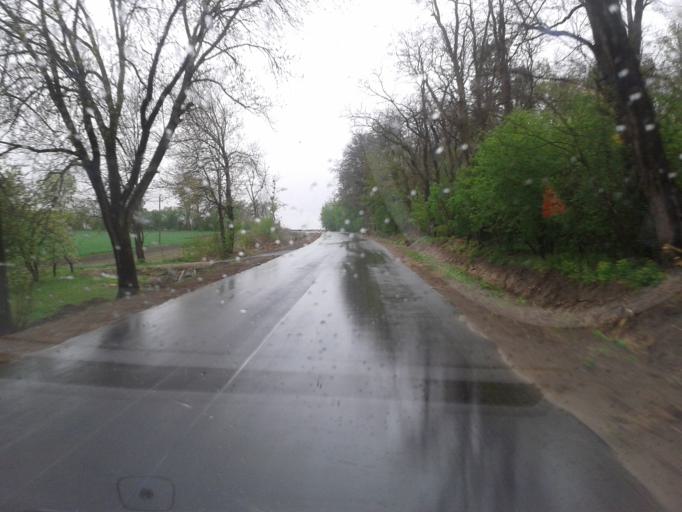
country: PL
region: Lublin Voivodeship
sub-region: Powiat tomaszowski
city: Lubycza Krolewska
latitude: 50.3645
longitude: 23.5678
